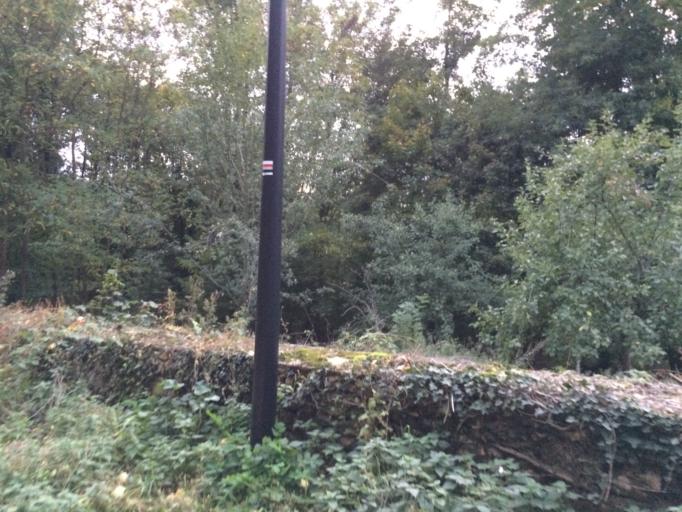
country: FR
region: Ile-de-France
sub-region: Departement des Yvelines
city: Velizy-Villacoublay
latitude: 48.7622
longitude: 2.1951
